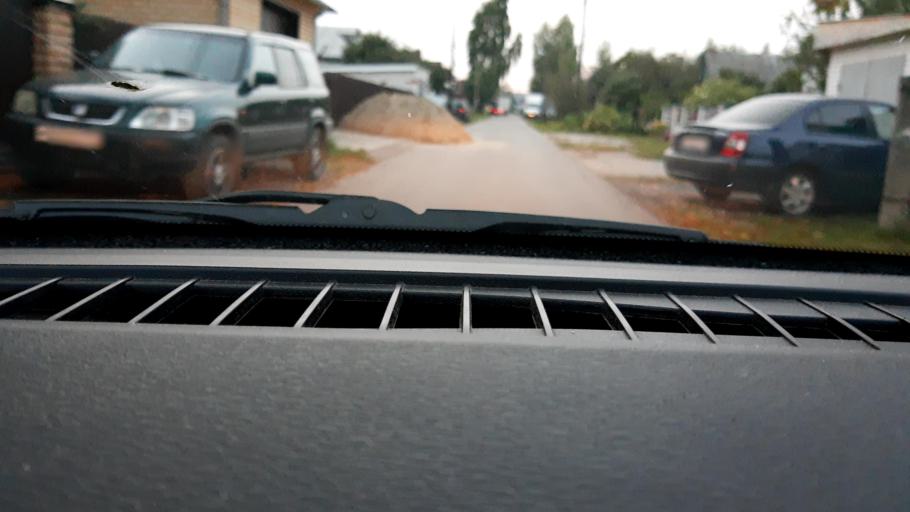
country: RU
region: Nizjnij Novgorod
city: Kstovo
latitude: 56.1726
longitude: 44.1720
